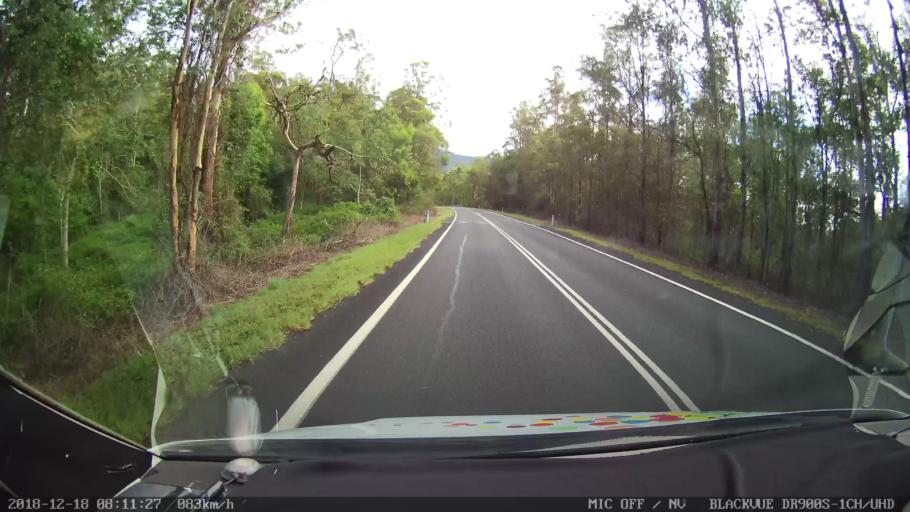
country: AU
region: New South Wales
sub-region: Kyogle
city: Kyogle
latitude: -28.3508
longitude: 152.6690
